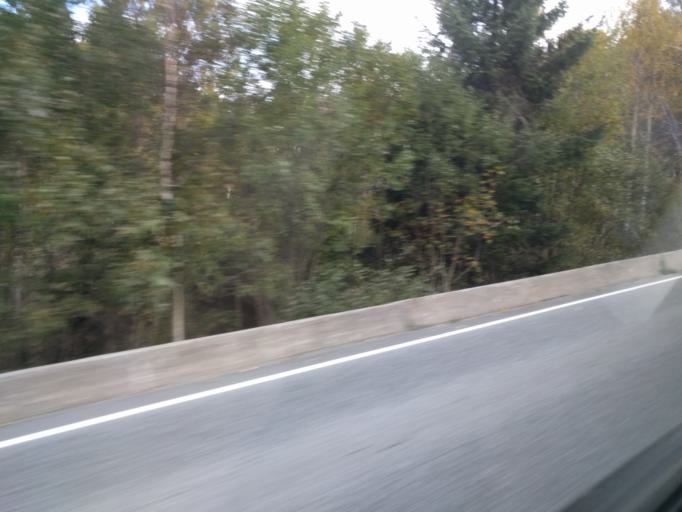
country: NO
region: Vest-Agder
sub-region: Songdalen
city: Nodeland
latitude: 58.2536
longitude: 7.8488
